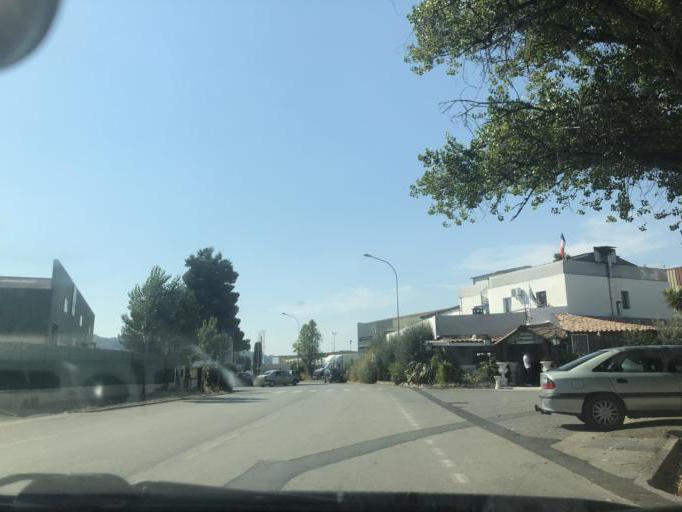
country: FR
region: Provence-Alpes-Cote d'Azur
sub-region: Departement des Alpes-Maritimes
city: Castagniers
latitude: 43.7817
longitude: 7.2112
